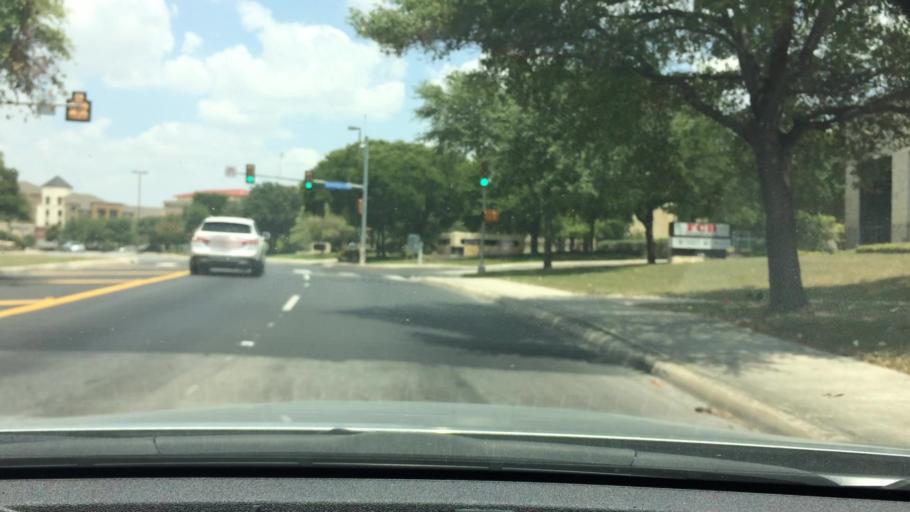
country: US
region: Texas
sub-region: Bexar County
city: Olmos Park
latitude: 29.4919
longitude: -98.4805
